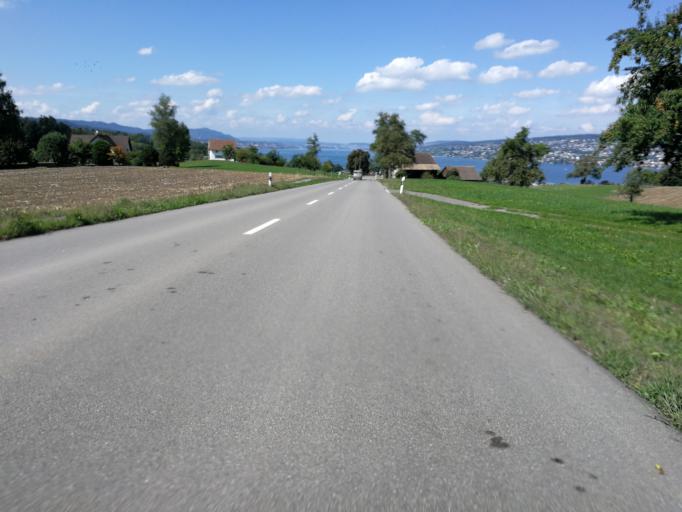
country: CH
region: Zurich
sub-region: Bezirk Horgen
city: Au / Unter-Dorf
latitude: 47.2436
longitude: 8.6237
